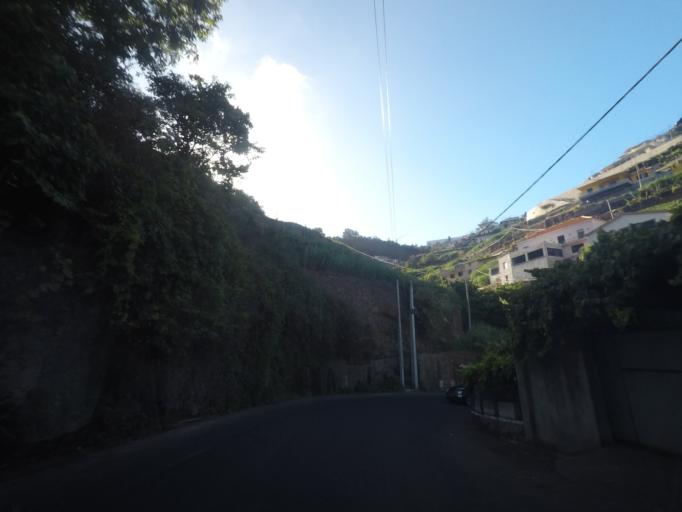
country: PT
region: Madeira
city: Camara de Lobos
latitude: 32.6655
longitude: -16.9917
